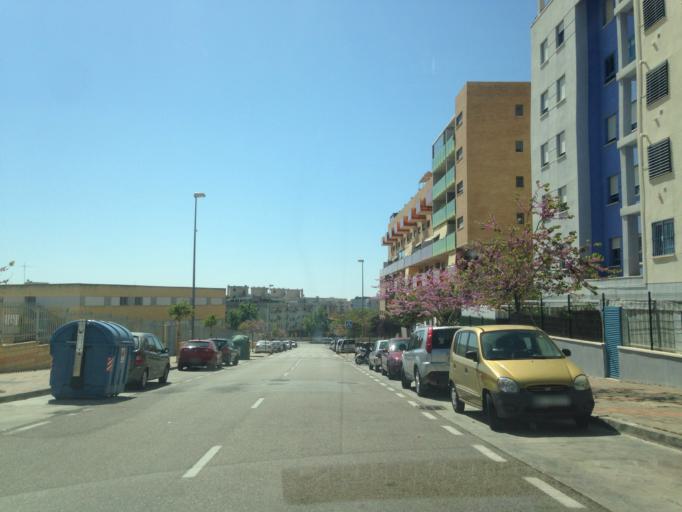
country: ES
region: Andalusia
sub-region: Provincia de Malaga
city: Malaga
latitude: 36.7258
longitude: -4.4824
